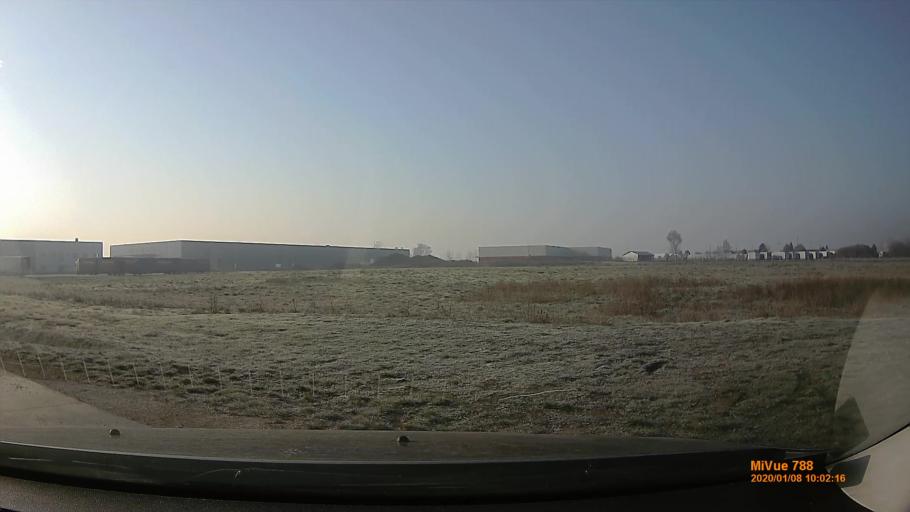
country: HU
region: Bacs-Kiskun
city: Kecskemet
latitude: 46.8765
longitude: 19.7051
